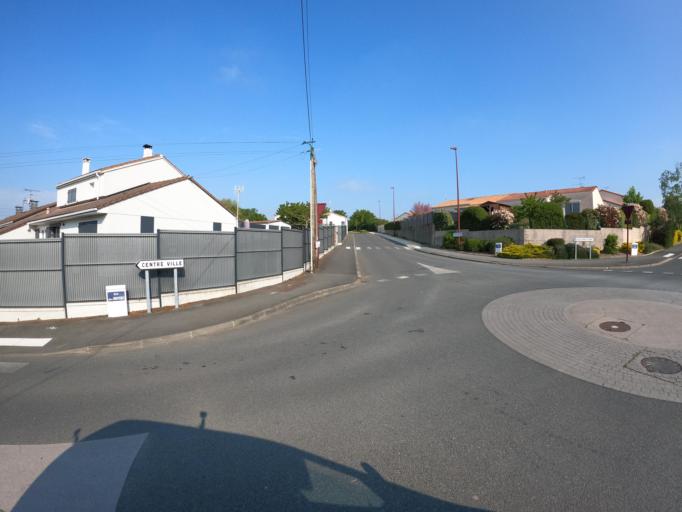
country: FR
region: Pays de la Loire
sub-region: Departement de Maine-et-Loire
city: La Seguiniere
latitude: 47.0656
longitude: -0.9454
